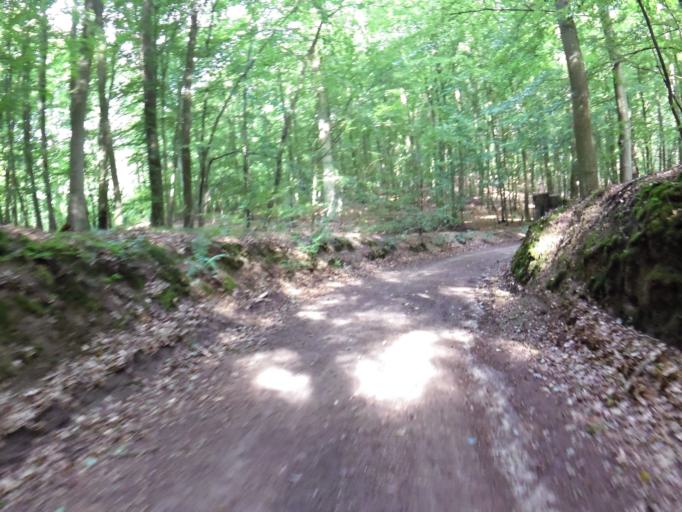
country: DE
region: Mecklenburg-Vorpommern
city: Seebad Bansin
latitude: 53.9539
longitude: 14.1061
